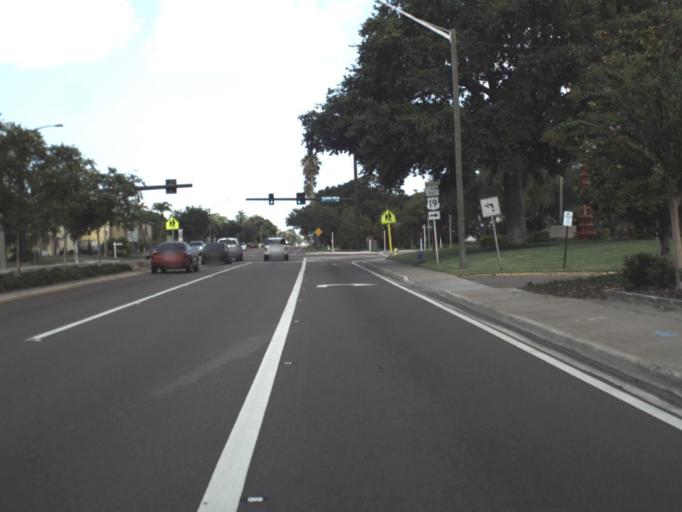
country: US
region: Florida
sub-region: Pinellas County
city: Gulfport
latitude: 27.7773
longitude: -82.7133
